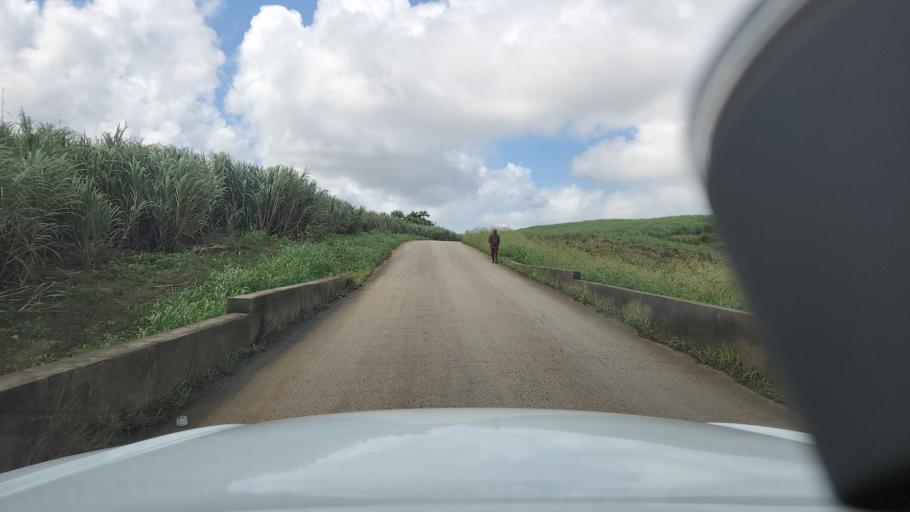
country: BB
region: Saint Joseph
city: Bathsheba
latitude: 13.1953
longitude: -59.5208
